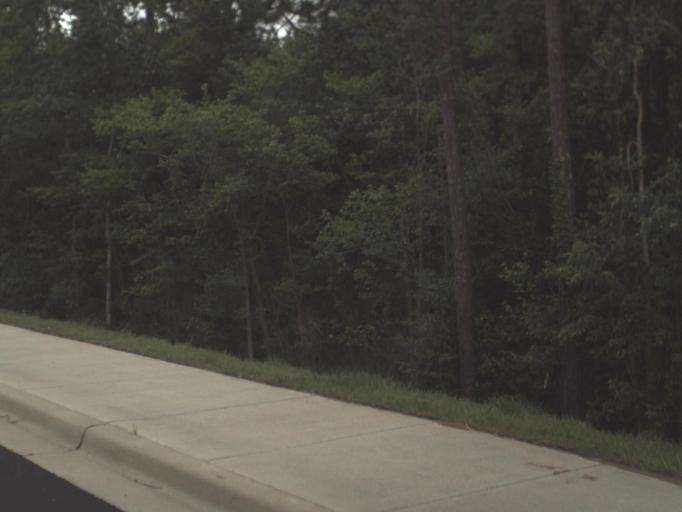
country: US
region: Florida
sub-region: Santa Rosa County
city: Bagdad
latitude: 30.5542
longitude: -87.0870
